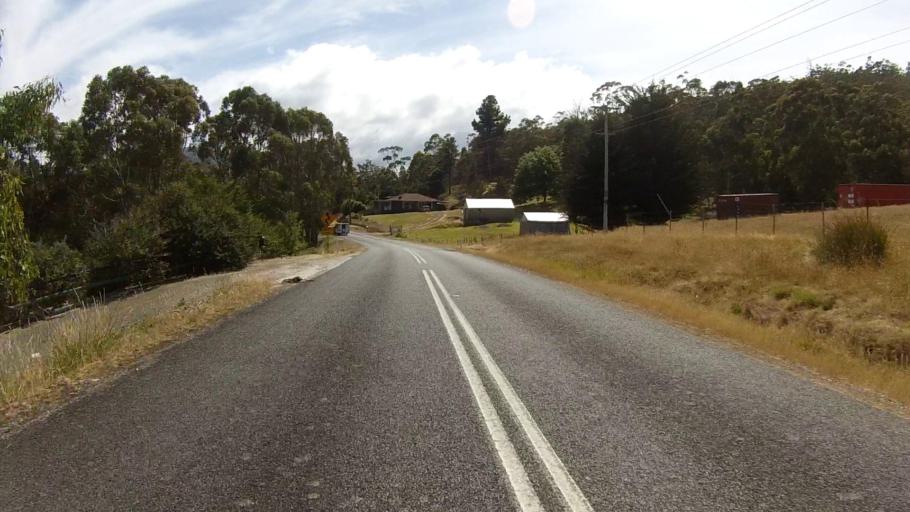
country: AU
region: Tasmania
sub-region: Huon Valley
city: Cygnet
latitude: -43.2440
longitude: 147.1504
